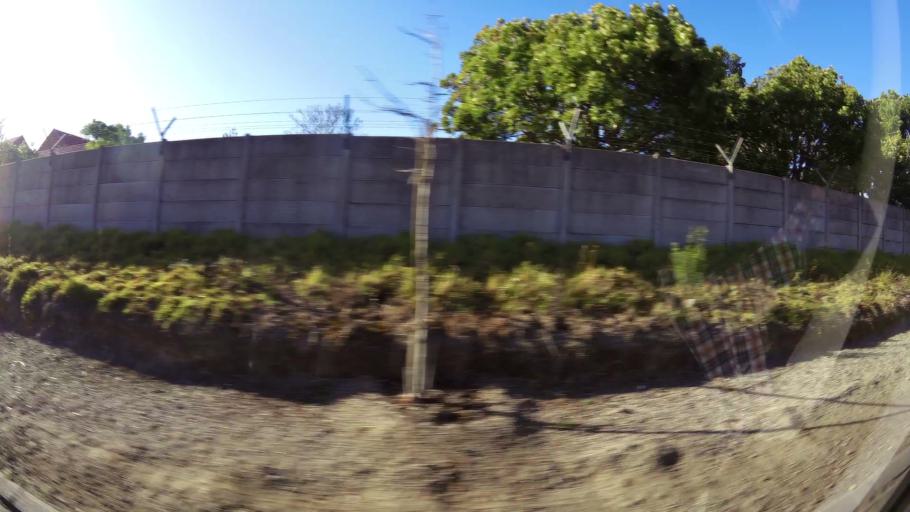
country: ZA
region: Western Cape
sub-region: Eden District Municipality
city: George
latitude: -33.9560
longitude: 22.4463
